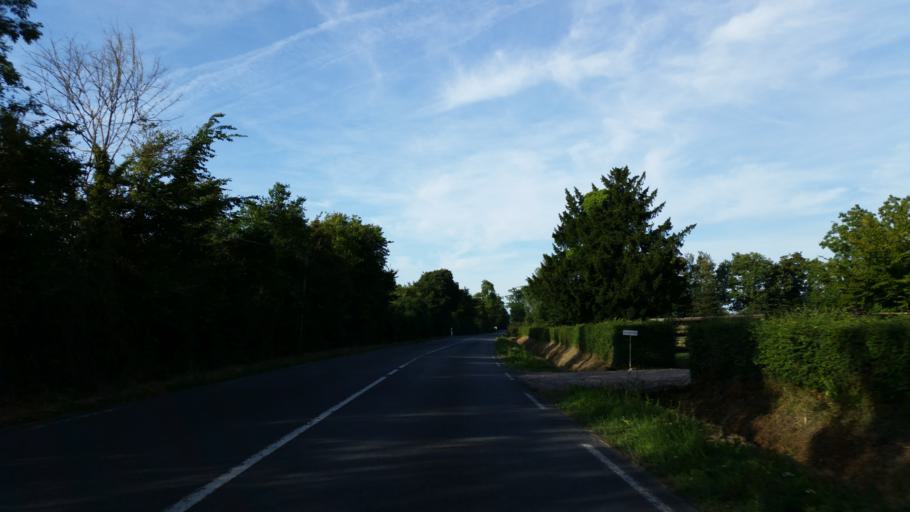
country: FR
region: Lower Normandy
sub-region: Departement du Calvados
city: Cambremer
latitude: 49.1707
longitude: 0.0067
